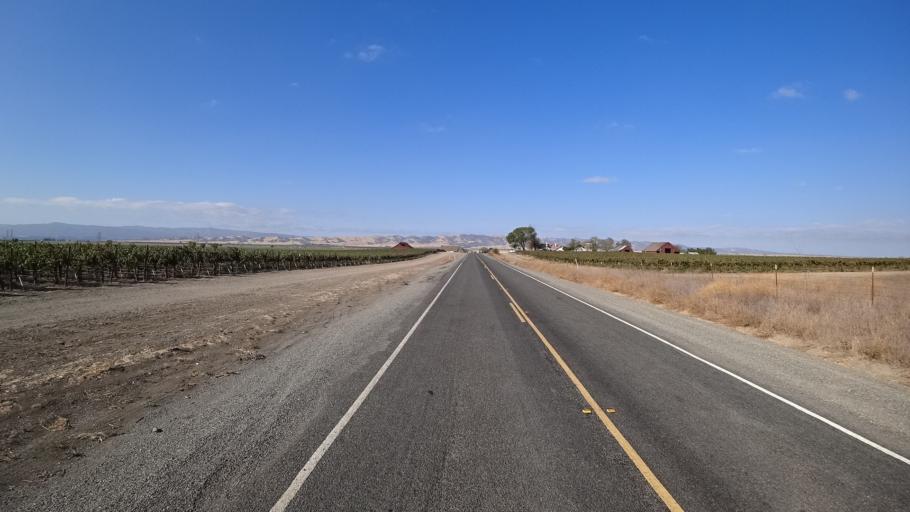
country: US
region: California
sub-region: Yolo County
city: Esparto
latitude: 38.7808
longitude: -122.0020
